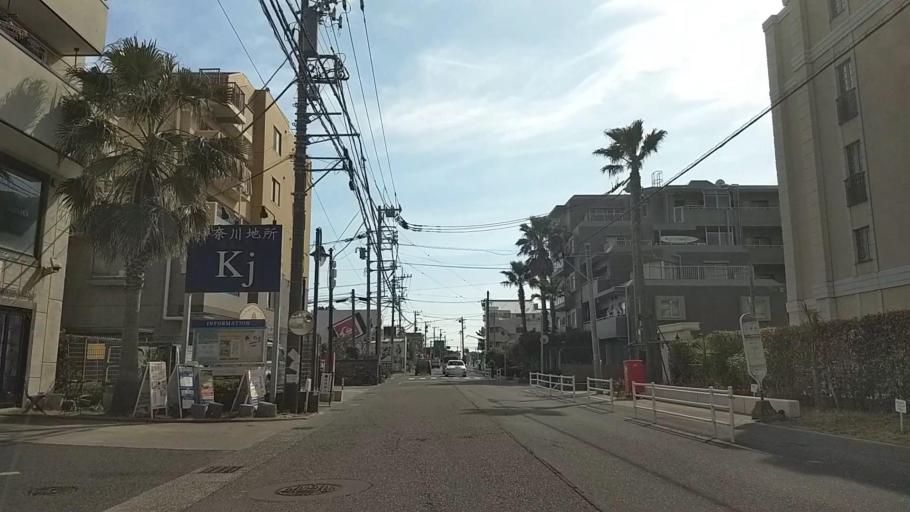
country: JP
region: Kanagawa
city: Fujisawa
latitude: 35.3215
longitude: 139.4539
